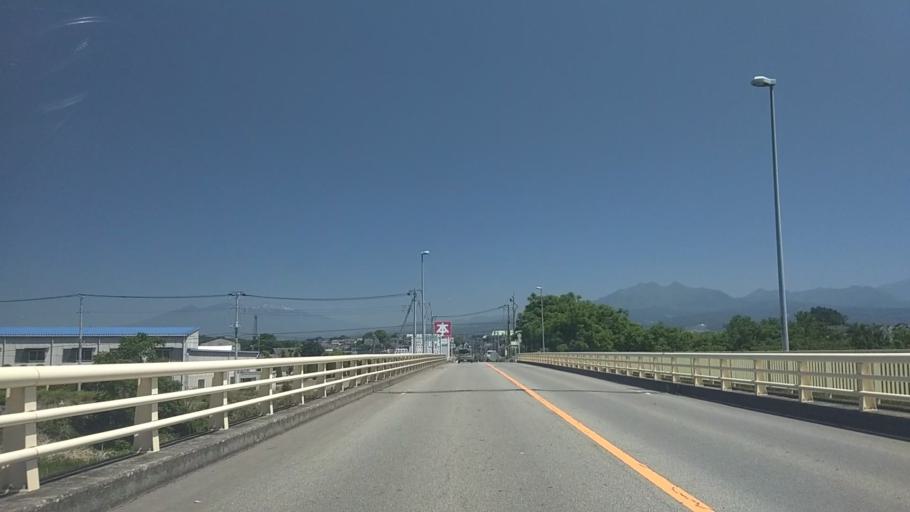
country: JP
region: Yamanashi
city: Nirasaki
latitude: 35.6716
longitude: 138.4648
